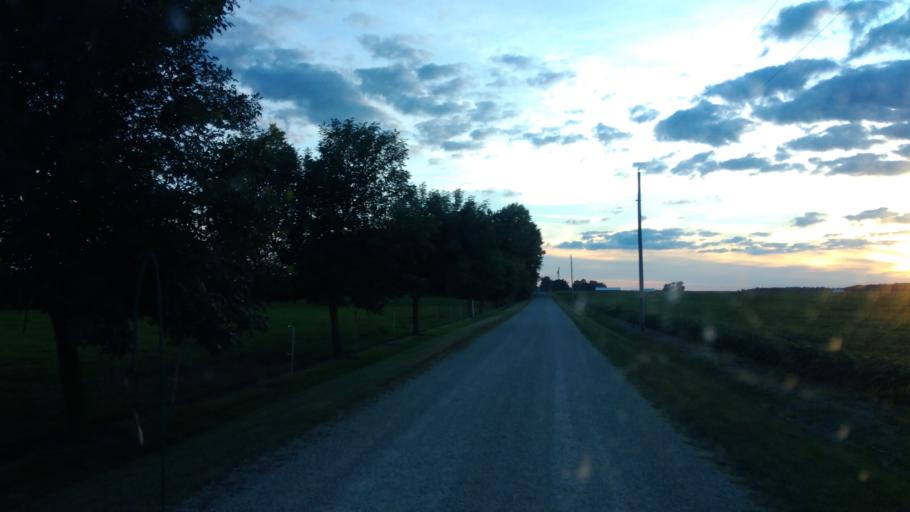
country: US
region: Indiana
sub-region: Adams County
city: Geneva
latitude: 40.6266
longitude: -85.0609
